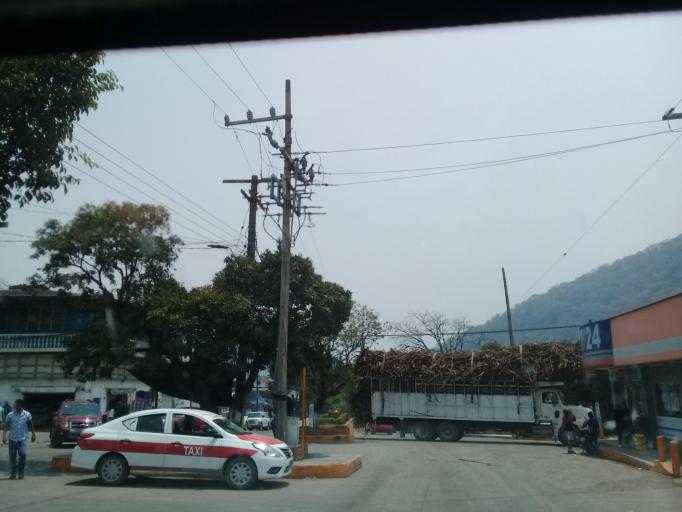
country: MX
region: Veracruz
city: Cosolapa
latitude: 18.6035
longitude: -96.6874
